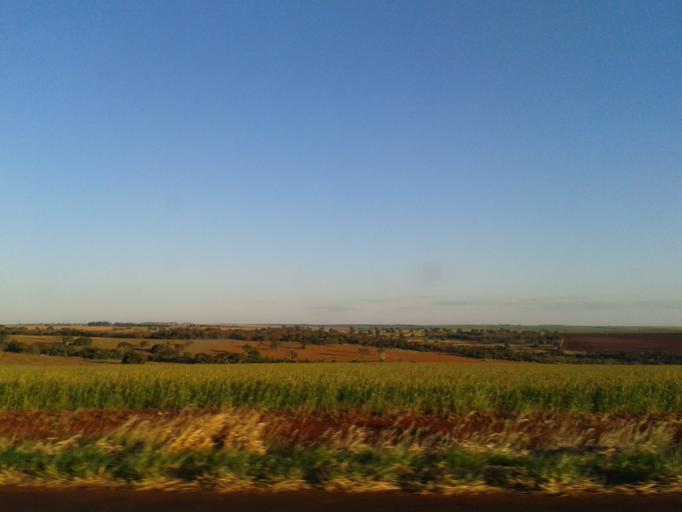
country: BR
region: Minas Gerais
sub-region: Centralina
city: Centralina
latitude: -18.7332
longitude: -49.2469
